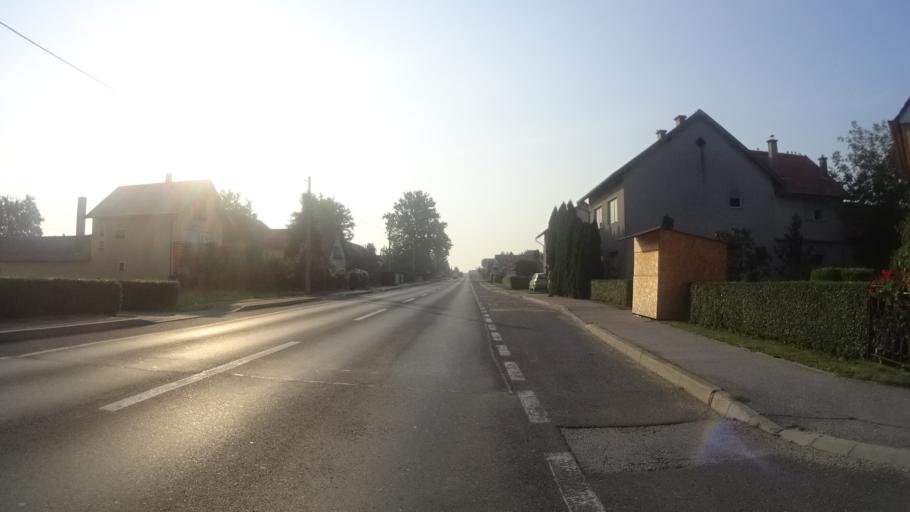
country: HR
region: Varazdinska
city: Petrijanec
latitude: 46.3443
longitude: 16.2330
